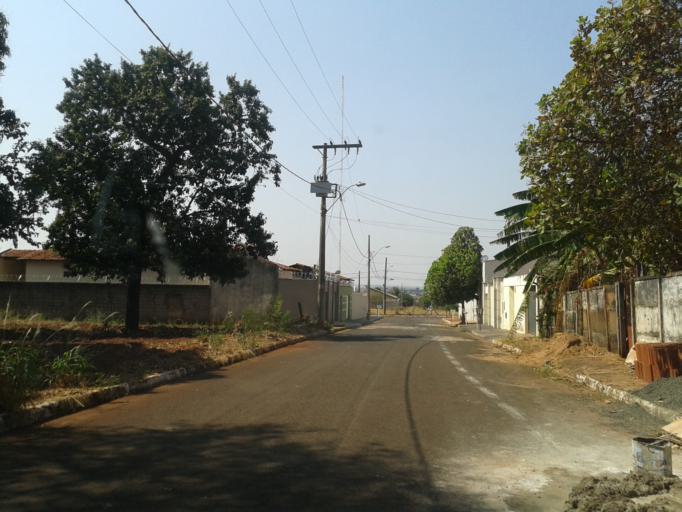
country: BR
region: Minas Gerais
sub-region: Ituiutaba
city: Ituiutaba
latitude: -18.9738
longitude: -49.4752
